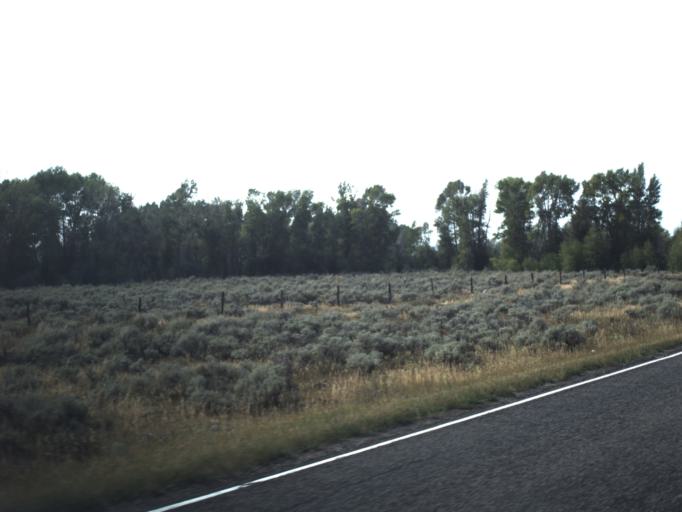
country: US
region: Wyoming
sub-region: Uinta County
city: Evanston
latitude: 40.9935
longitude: -110.8626
